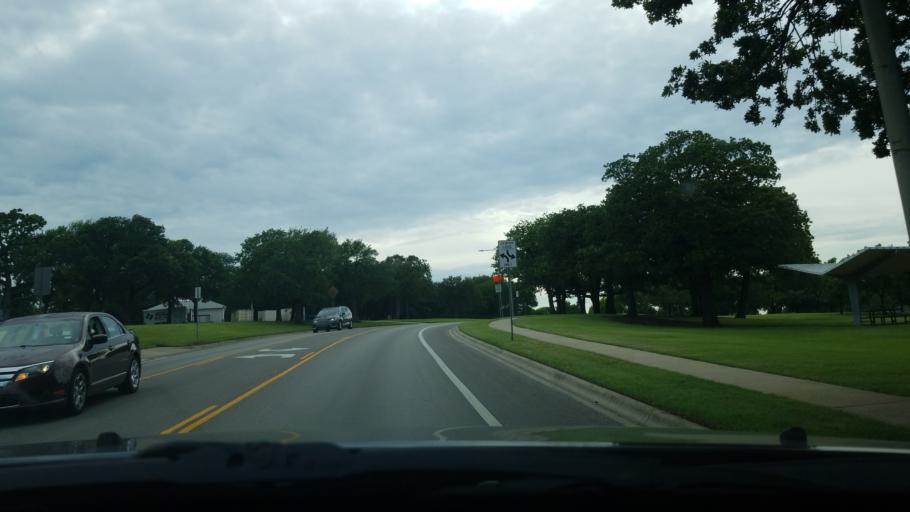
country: US
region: Texas
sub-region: Denton County
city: Denton
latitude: 33.2442
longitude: -97.1323
